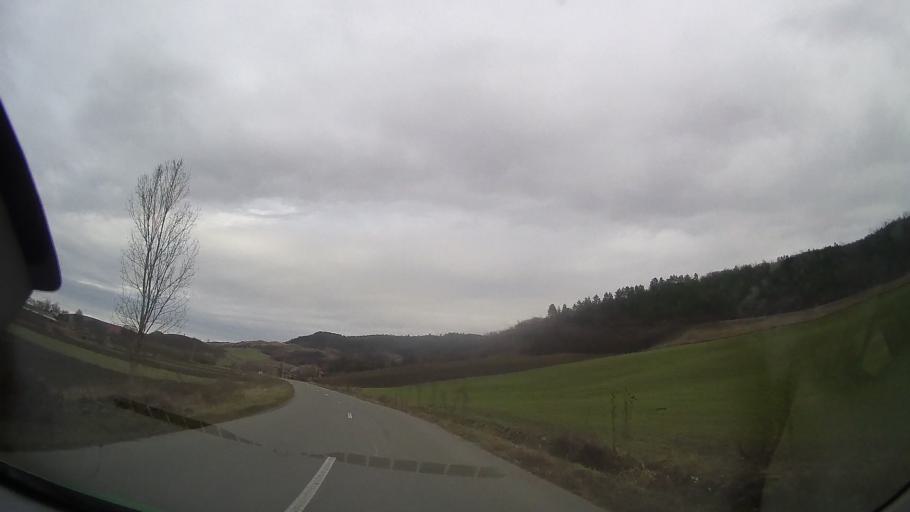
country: RO
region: Mures
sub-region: Comuna Faragau
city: Faragau
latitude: 46.7307
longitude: 24.5443
